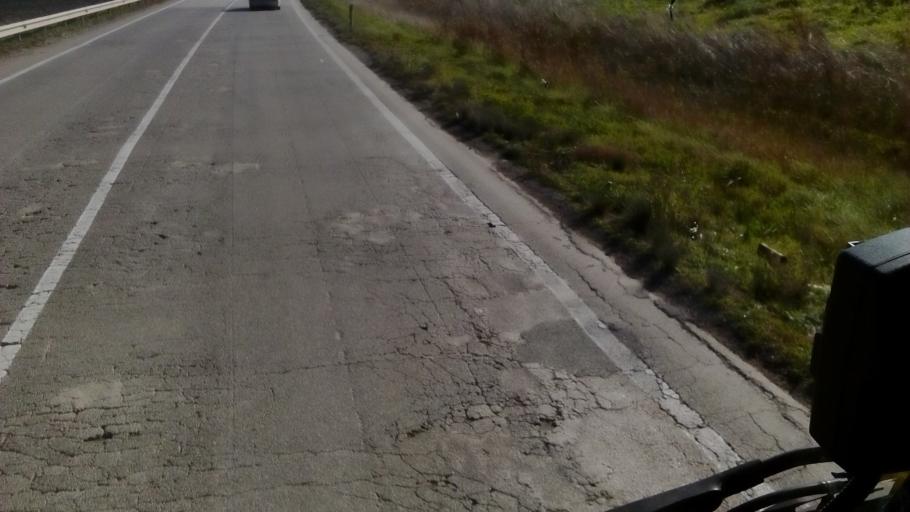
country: IT
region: Apulia
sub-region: Provincia di Foggia
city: Candela
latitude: 41.1170
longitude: 15.5779
